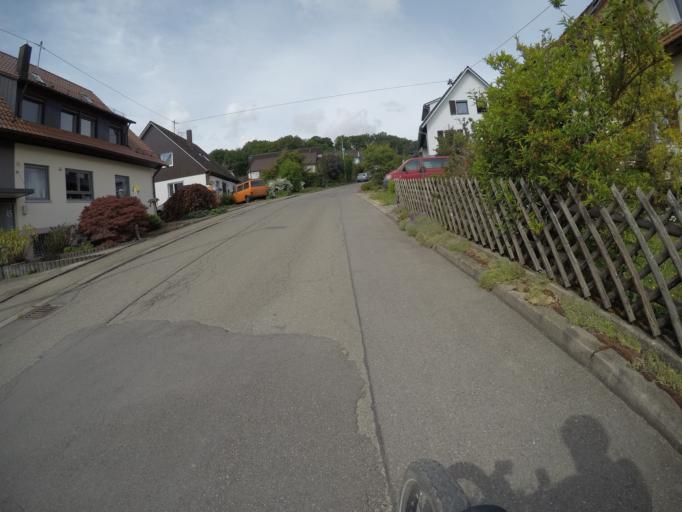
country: DE
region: Baden-Wuerttemberg
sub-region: Tuebingen Region
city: Tuebingen
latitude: 48.5418
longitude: 9.0082
